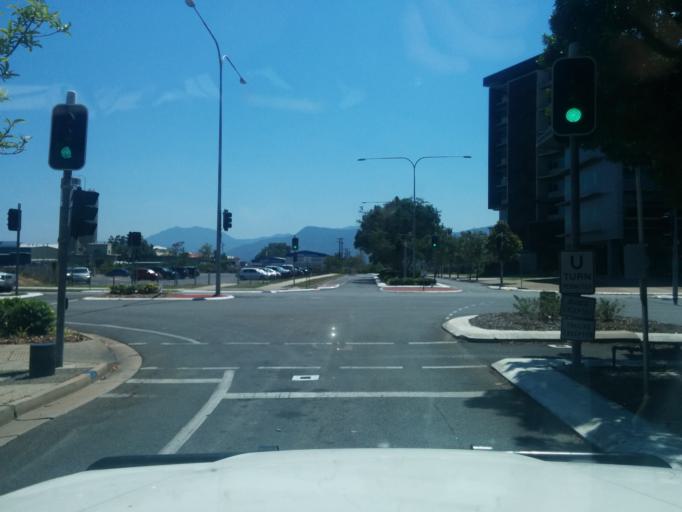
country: AU
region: Queensland
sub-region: Cairns
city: Cairns
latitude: -16.9273
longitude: 145.7771
